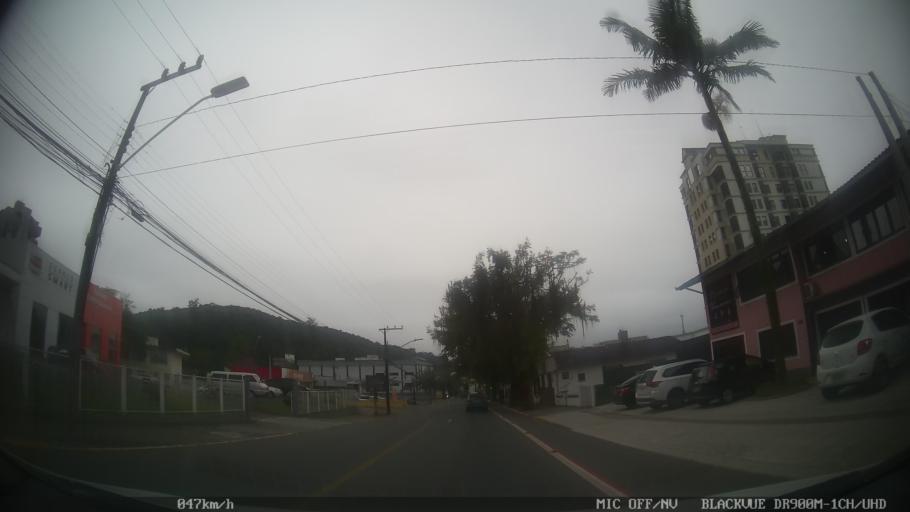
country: BR
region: Santa Catarina
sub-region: Joinville
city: Joinville
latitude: -26.2921
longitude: -48.8407
